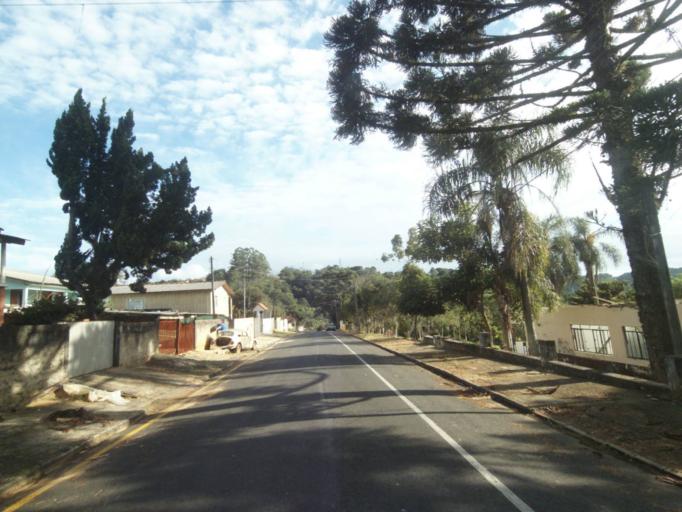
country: BR
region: Parana
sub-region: Telemaco Borba
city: Telemaco Borba
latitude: -24.3451
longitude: -50.6108
